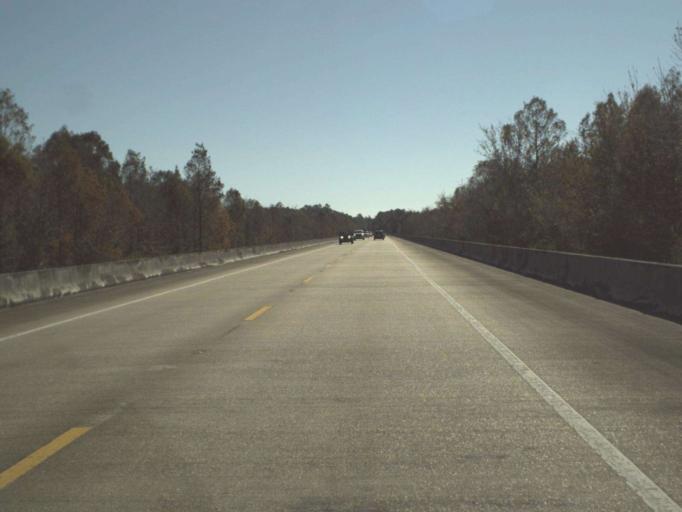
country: US
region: Florida
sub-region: Santa Rosa County
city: East Milton
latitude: 30.5756
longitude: -86.9266
